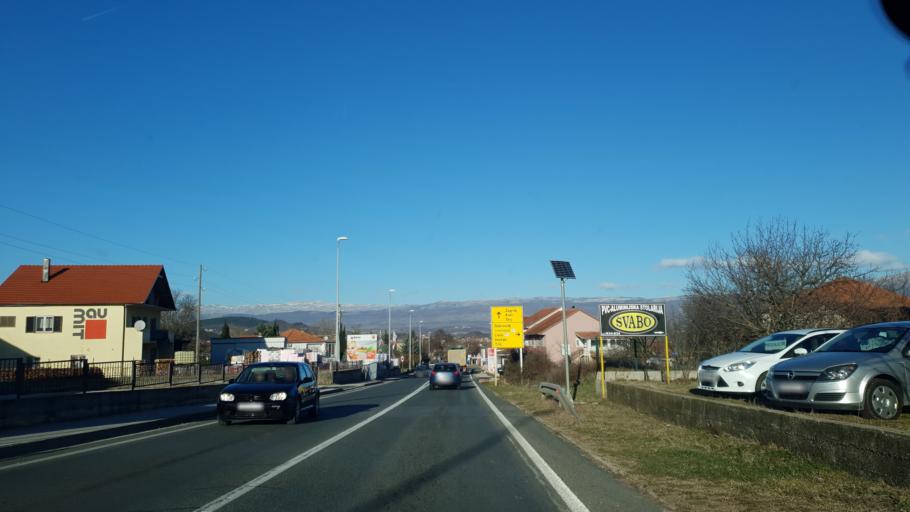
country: HR
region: Splitsko-Dalmatinska
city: Brnaze
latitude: 43.6791
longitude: 16.6491
